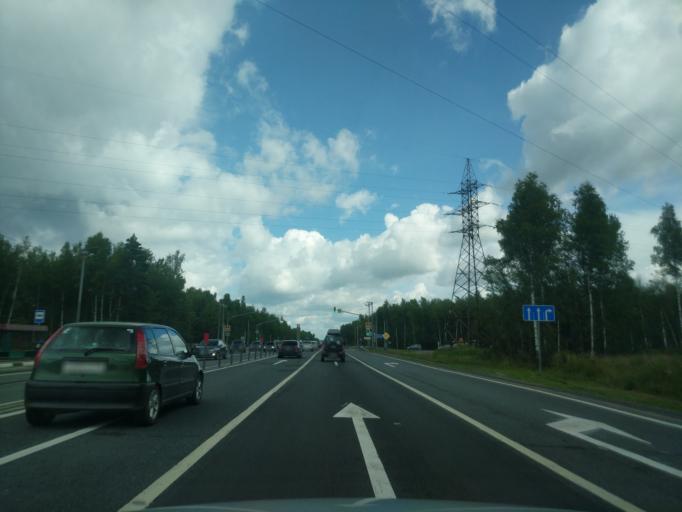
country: RU
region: Jaroslavl
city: Rostov
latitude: 57.2356
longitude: 39.4713
